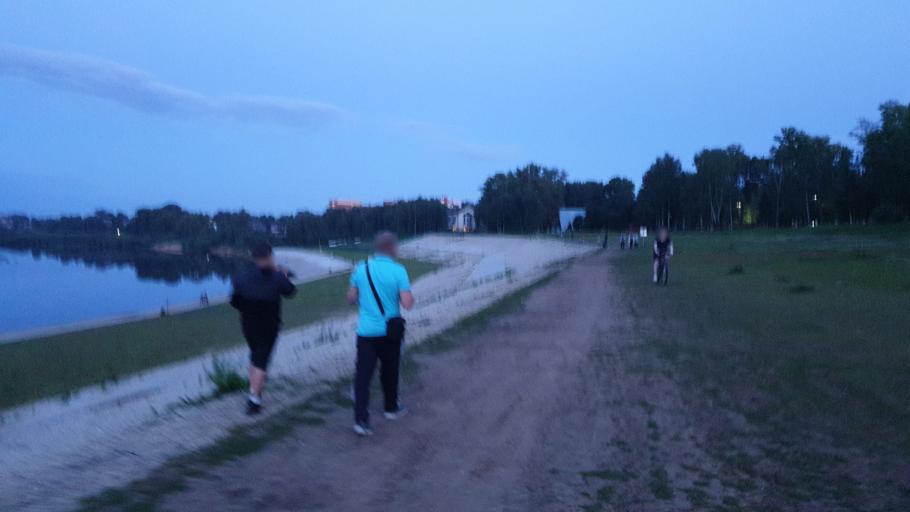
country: RU
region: Komi Republic
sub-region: Syktyvdinskiy Rayon
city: Syktyvkar
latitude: 61.6730
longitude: 50.8436
